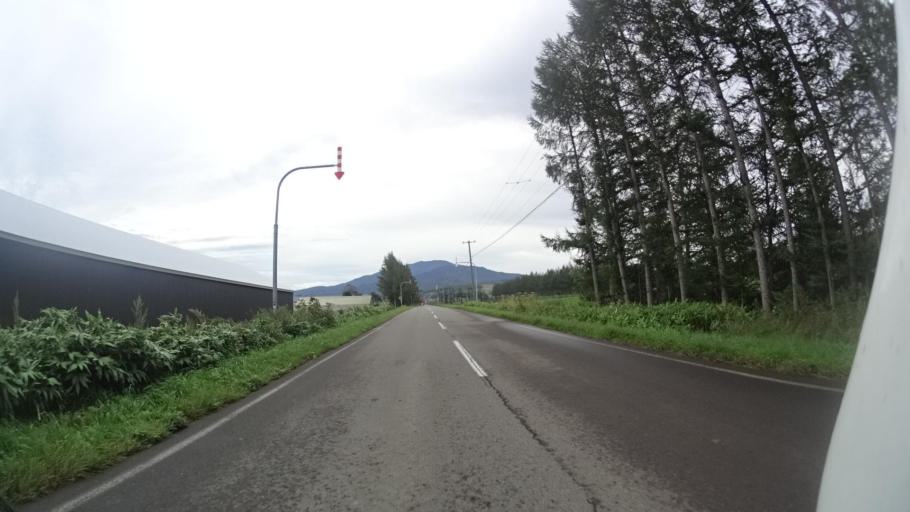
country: JP
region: Hokkaido
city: Shibetsu
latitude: 43.8737
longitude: 144.7307
